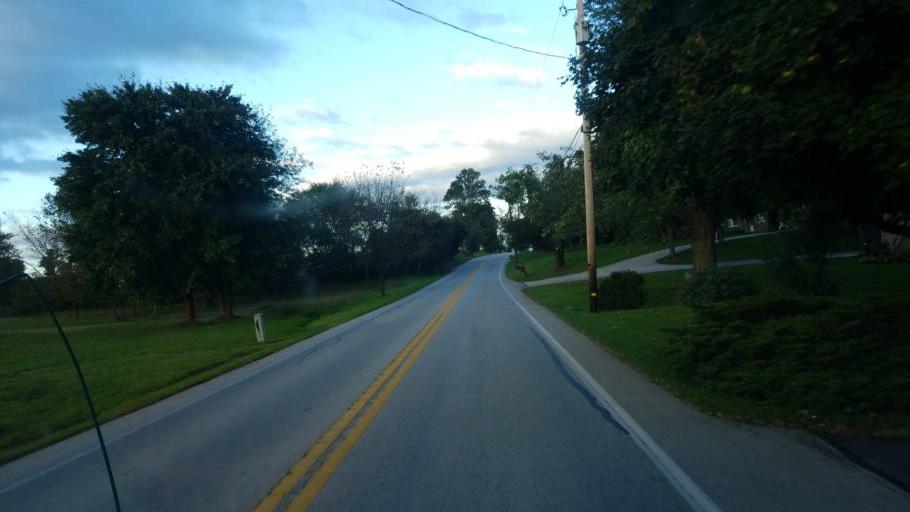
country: US
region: Pennsylvania
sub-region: Adams County
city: East Berlin
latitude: 39.9363
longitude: -76.9187
